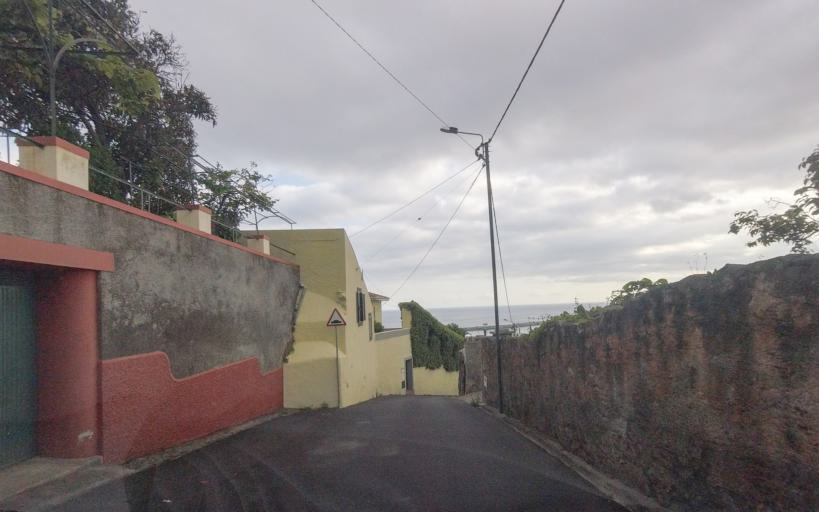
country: PT
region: Madeira
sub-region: Funchal
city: Nossa Senhora do Monte
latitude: 32.6540
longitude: -16.8996
